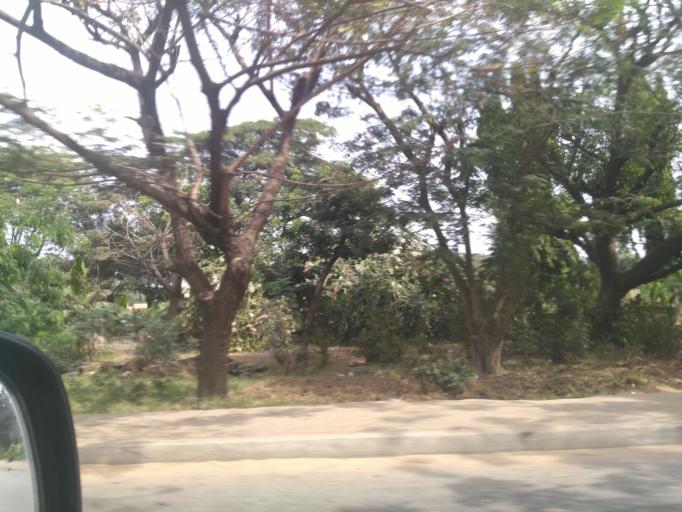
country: GH
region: Greater Accra
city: Accra
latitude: 5.5945
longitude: -0.1878
